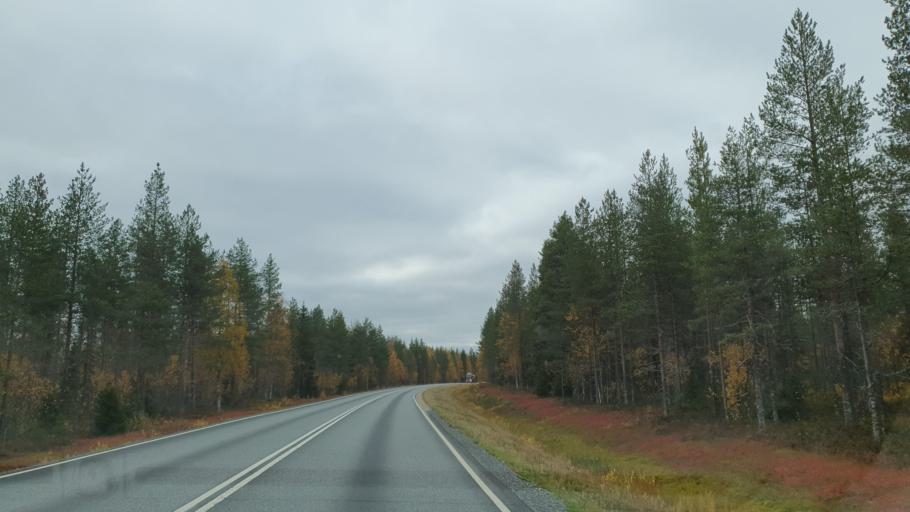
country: FI
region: Lapland
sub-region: Rovaniemi
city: Ranua
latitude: 66.0572
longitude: 26.3681
